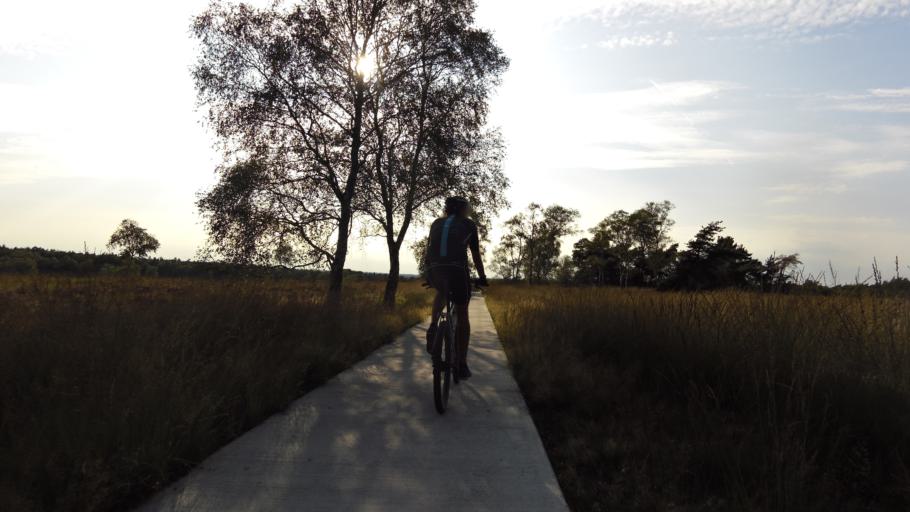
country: NL
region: Gelderland
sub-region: Gemeente Rozendaal
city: Rozendaal
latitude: 52.0394
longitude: 5.9657
